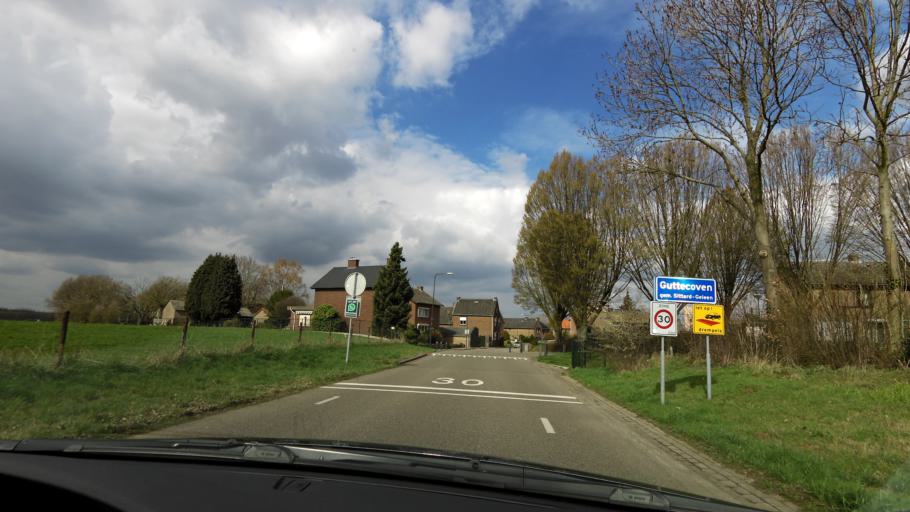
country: NL
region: Limburg
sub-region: Gemeente Sittard-Geleen
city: Limbricht
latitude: 51.0104
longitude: 5.8157
